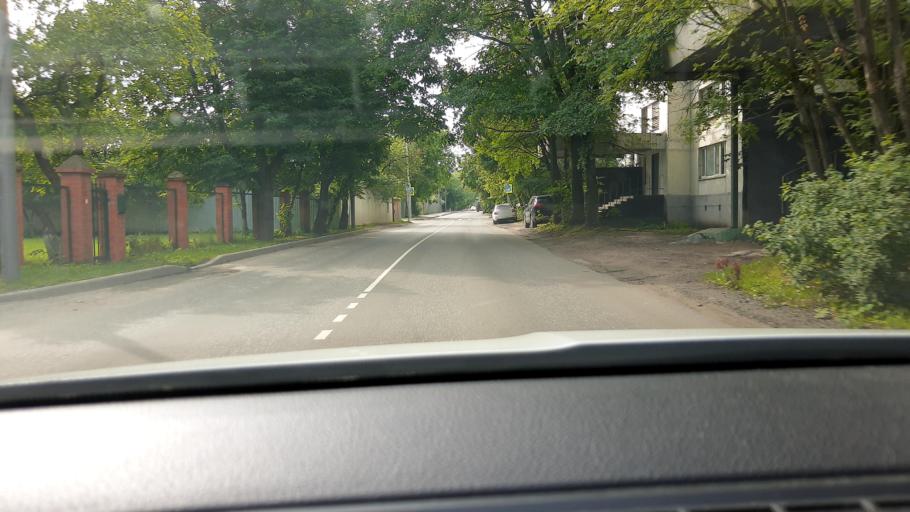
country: RU
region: Moskovskaya
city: Troitsk
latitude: 55.4892
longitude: 37.3048
